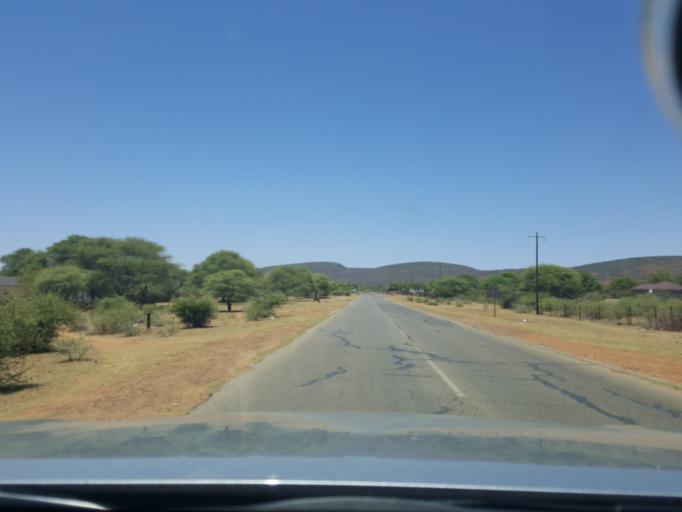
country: BW
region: South East
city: Lobatse
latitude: -25.2835
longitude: 25.9225
